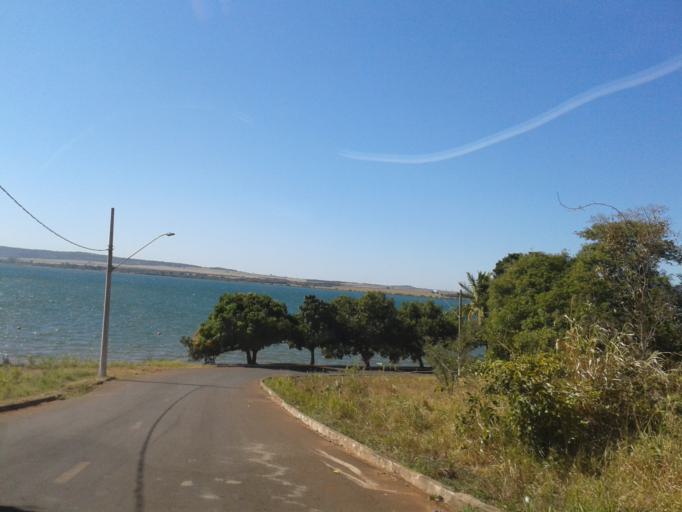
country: BR
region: Minas Gerais
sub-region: Capinopolis
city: Capinopolis
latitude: -18.5165
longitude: -49.4985
